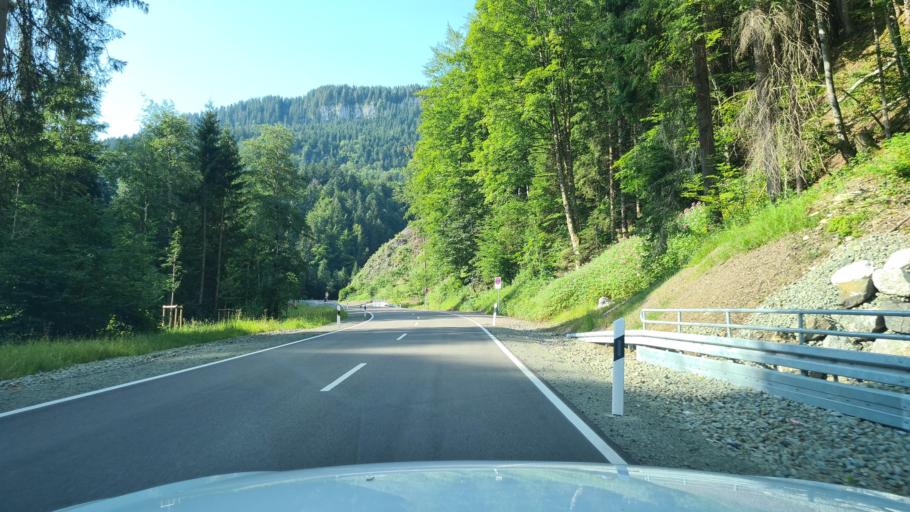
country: DE
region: Bavaria
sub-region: Swabia
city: Obermaiselstein
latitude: 47.4437
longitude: 10.2298
